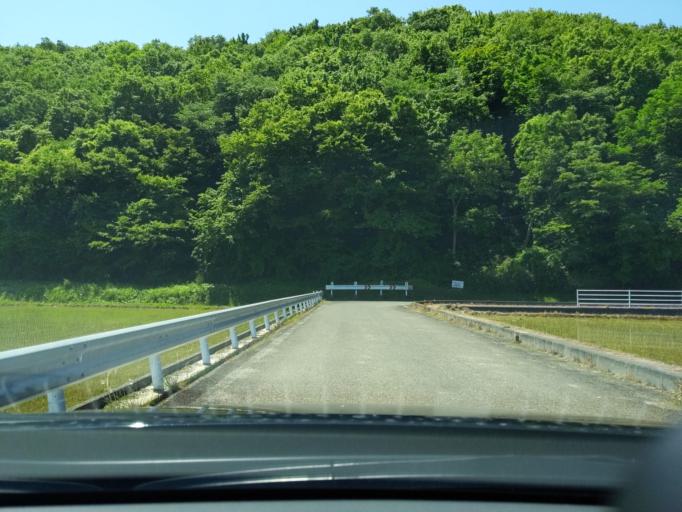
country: JP
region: Fukushima
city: Koriyama
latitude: 37.3897
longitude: 140.2789
